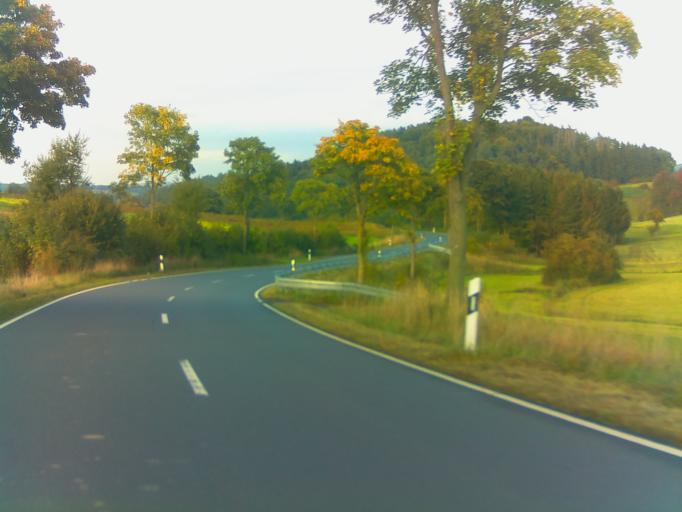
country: DE
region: Hesse
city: Reichelsheim
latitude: 49.7264
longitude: 8.8449
